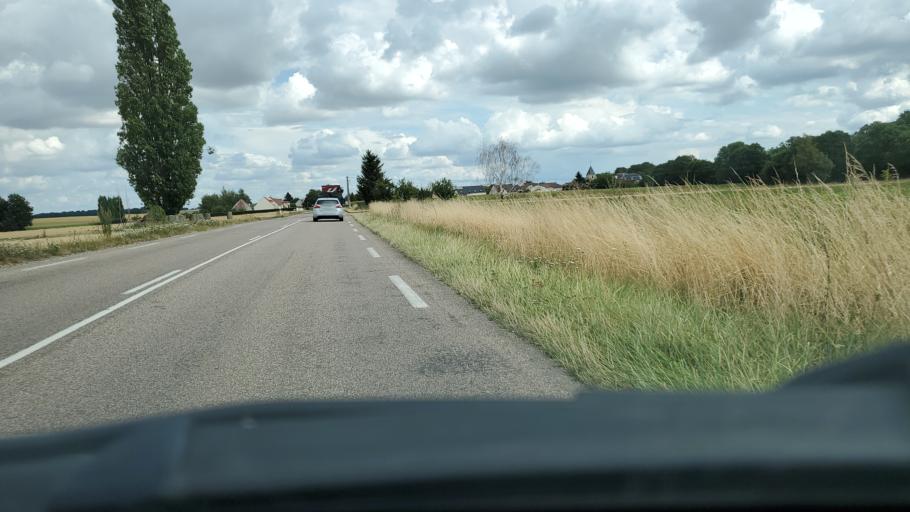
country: FR
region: Ile-de-France
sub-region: Departement de Seine-et-Marne
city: La Chapelle-sur-Crecy
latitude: 48.8896
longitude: 2.9526
